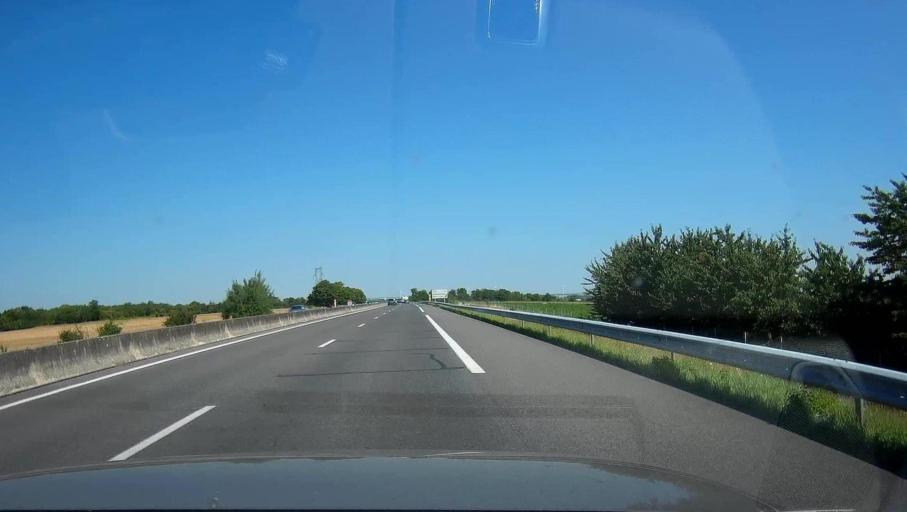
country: FR
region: Champagne-Ardenne
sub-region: Departement de l'Aube
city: Arcis-sur-Aube
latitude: 48.5121
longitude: 4.1722
